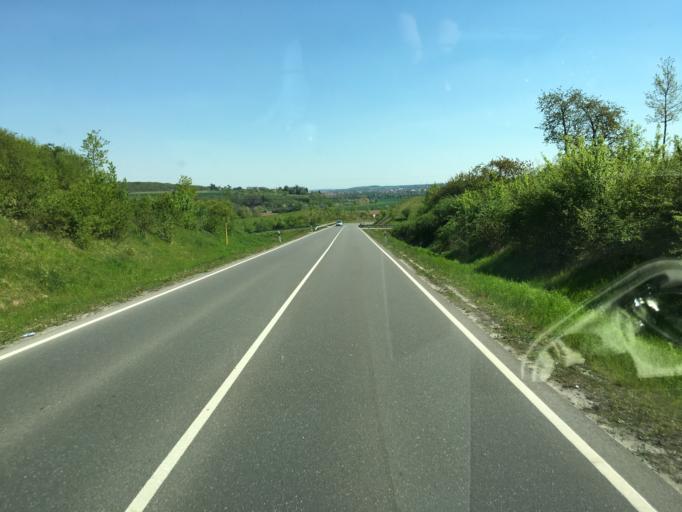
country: DE
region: Saxony-Anhalt
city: Freyburg
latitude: 51.1896
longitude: 11.7770
